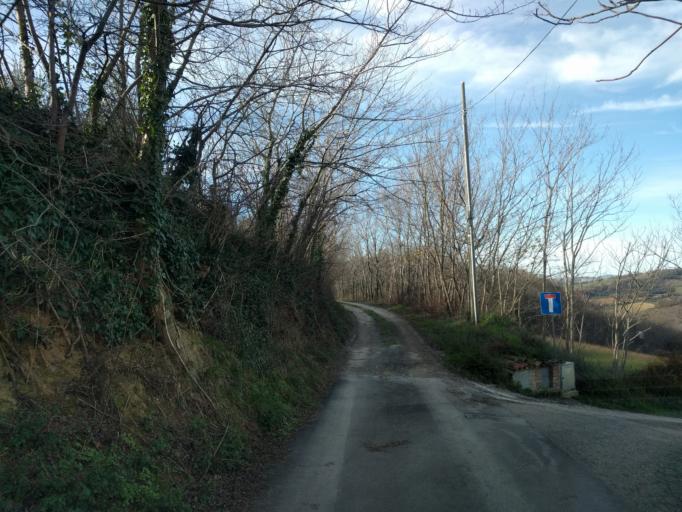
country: IT
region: The Marches
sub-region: Provincia di Pesaro e Urbino
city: Cuccurano
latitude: 43.8102
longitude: 12.9500
